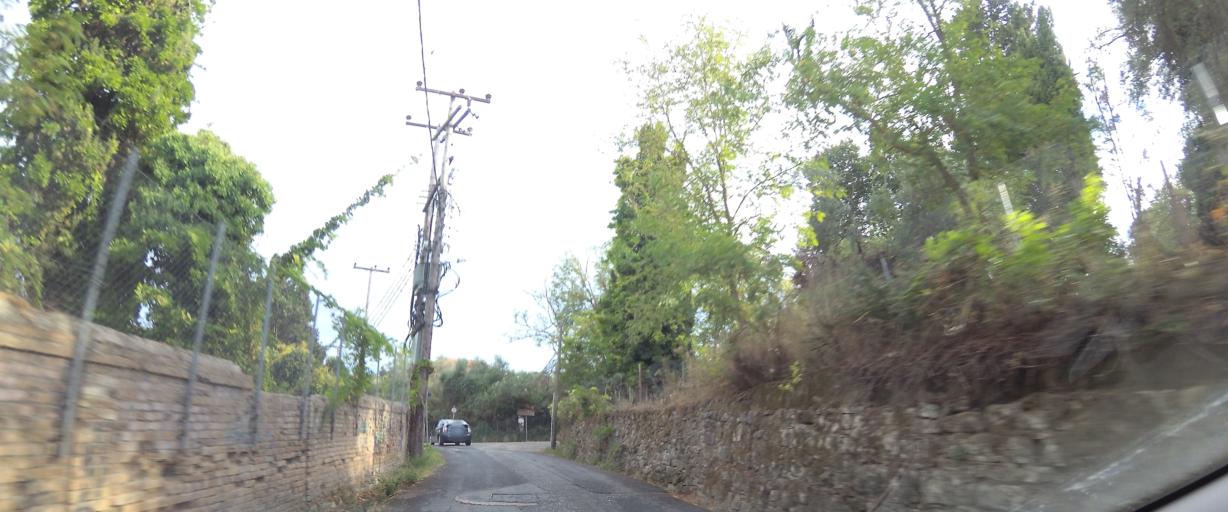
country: GR
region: Ionian Islands
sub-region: Nomos Kerkyras
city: Kerkyra
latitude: 39.6094
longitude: 19.9198
